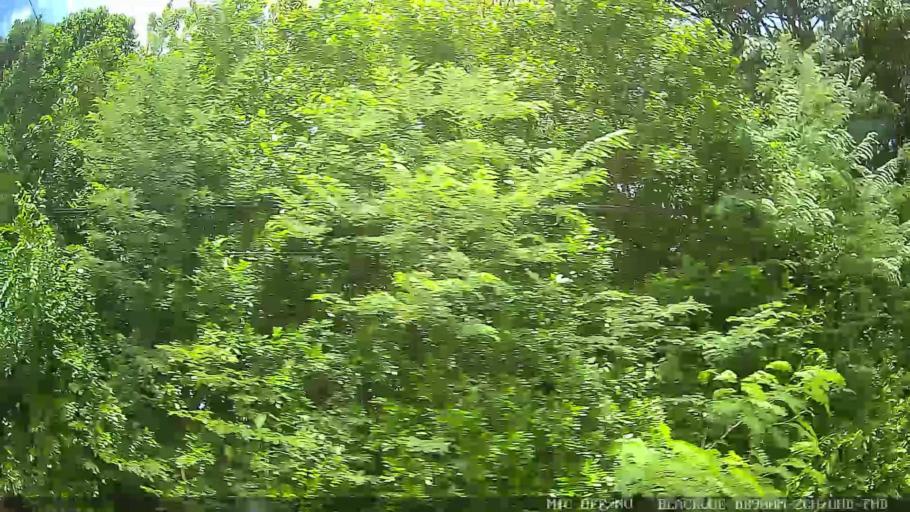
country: BR
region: Sao Paulo
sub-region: Jaguariuna
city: Jaguariuna
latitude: -22.6216
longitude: -47.0604
